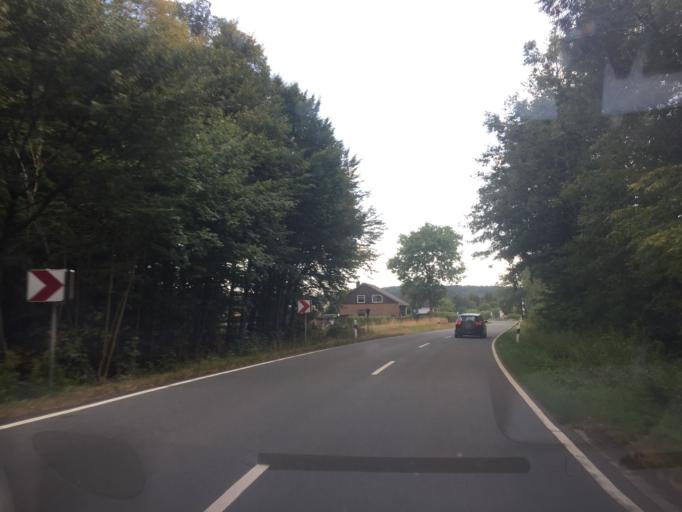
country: DE
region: Lower Saxony
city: Walkenried
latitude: 51.5954
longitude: 10.6202
